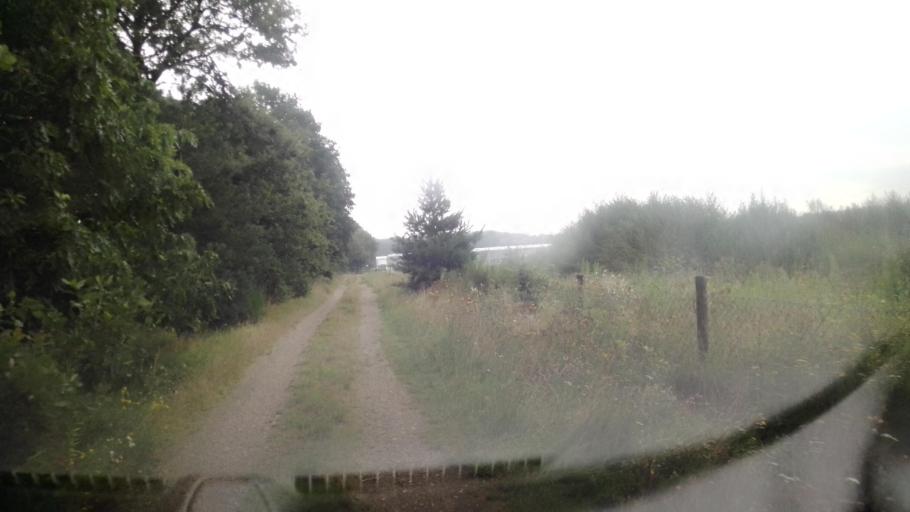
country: NL
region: Limburg
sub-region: Gemeente Venlo
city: Tegelen
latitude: 51.4068
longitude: 6.1115
